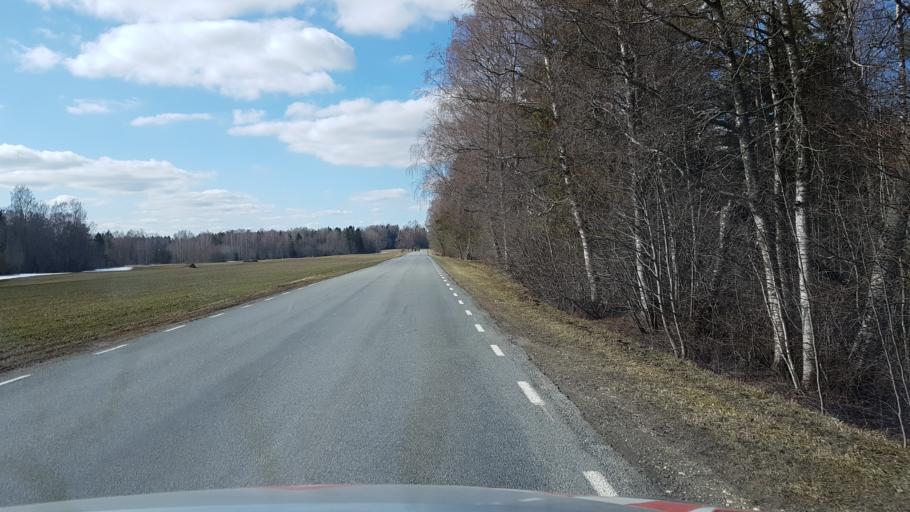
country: EE
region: Laeaene-Virumaa
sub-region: Tamsalu vald
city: Tamsalu
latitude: 59.1661
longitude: 26.0736
